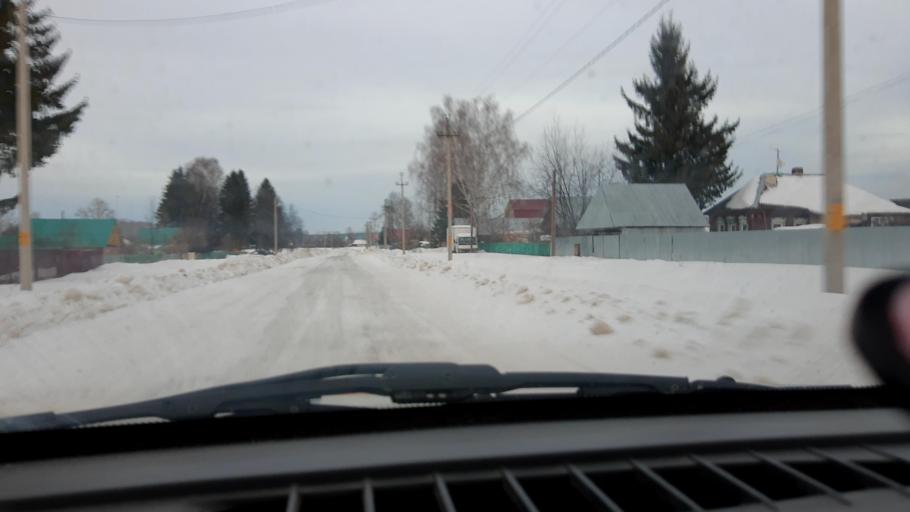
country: RU
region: Bashkortostan
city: Urman
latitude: 54.8699
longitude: 56.8685
